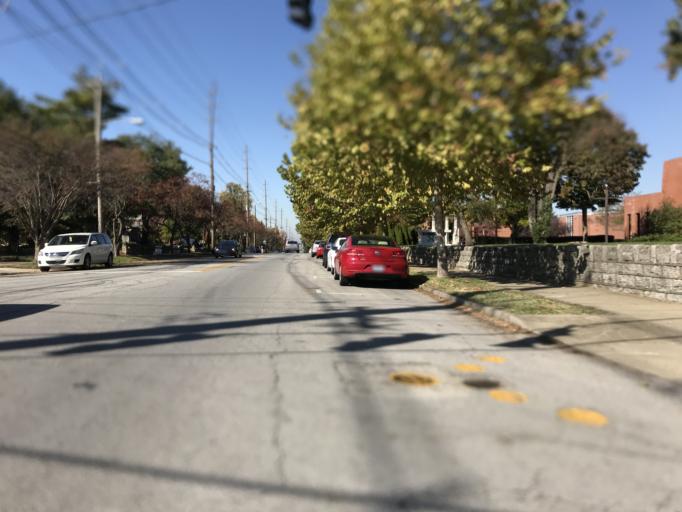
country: US
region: Indiana
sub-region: Clark County
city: Jeffersonville
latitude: 38.2556
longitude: -85.7127
